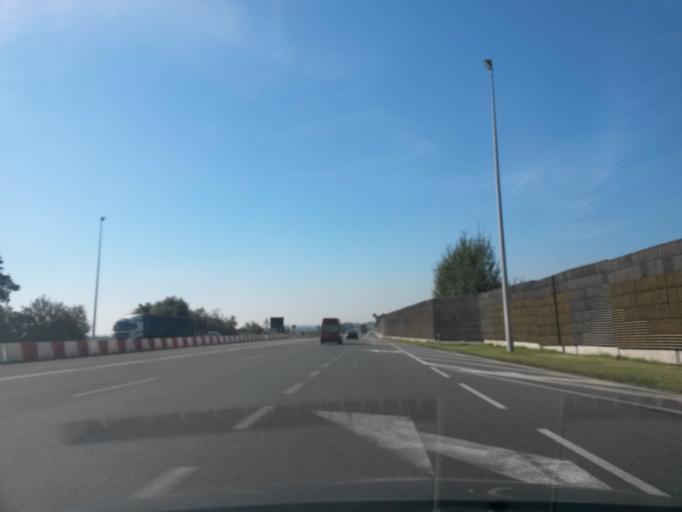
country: PL
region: Lesser Poland Voivodeship
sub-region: Powiat krakowski
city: Balice
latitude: 50.0829
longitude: 19.7882
